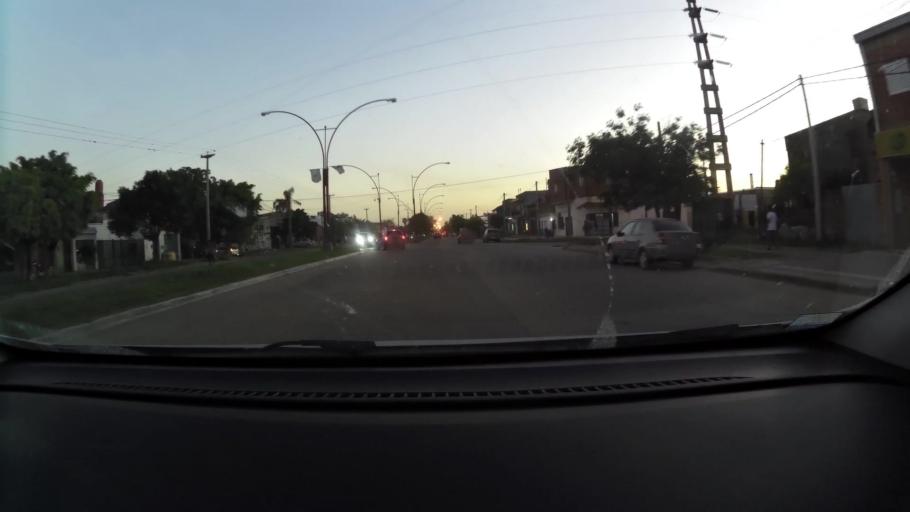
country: AR
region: Santa Fe
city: Santa Fe de la Vera Cruz
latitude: -31.6078
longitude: -60.7131
